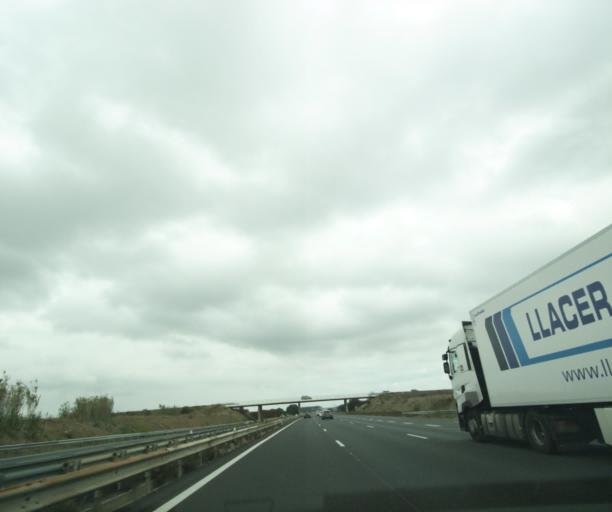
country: FR
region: Languedoc-Roussillon
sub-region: Departement de l'Herault
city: Bessan
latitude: 43.3768
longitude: 3.4185
